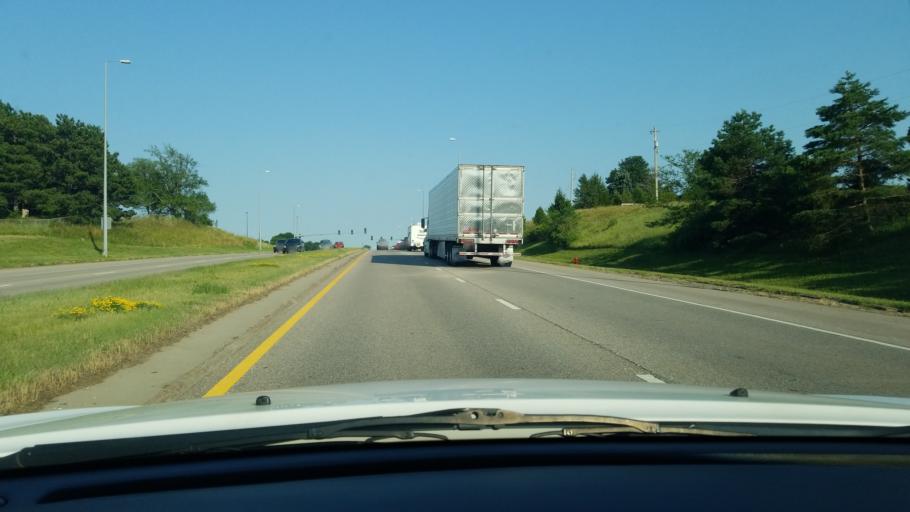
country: US
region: Nebraska
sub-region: Lancaster County
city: Lincoln
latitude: 40.7472
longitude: -96.6274
